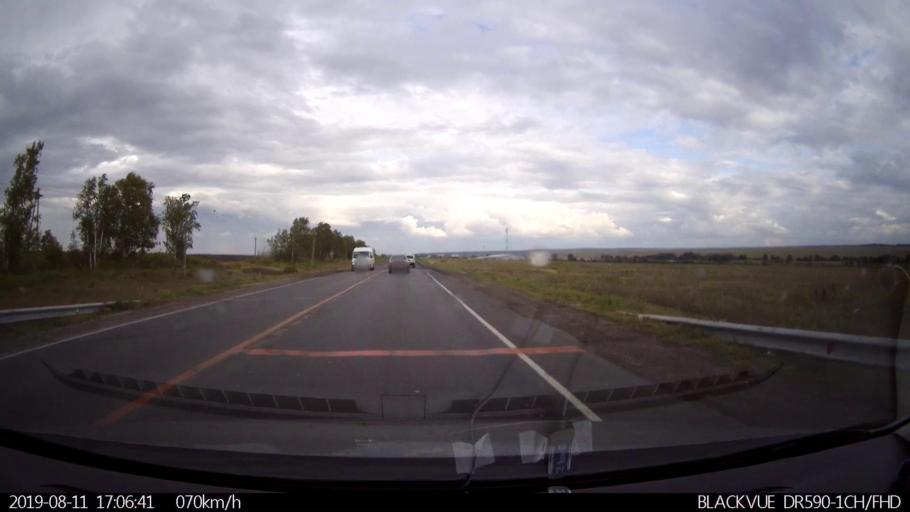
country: RU
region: Ulyanovsk
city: Mayna
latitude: 54.2943
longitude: 47.8108
